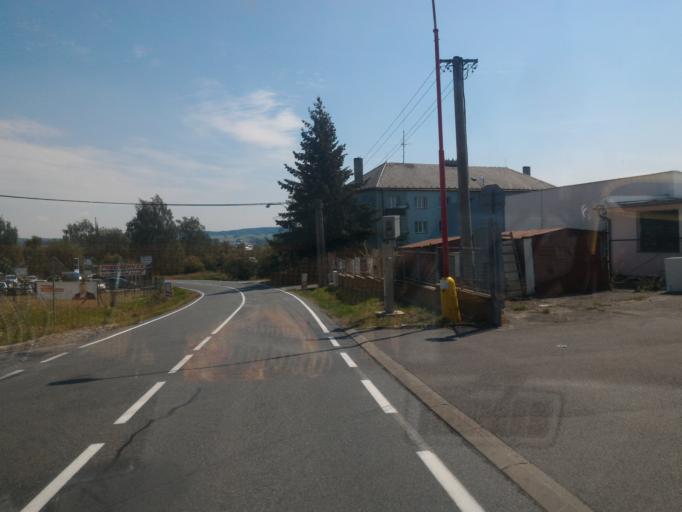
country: CZ
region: Pardubicky
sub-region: Okres Chrudim
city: Hlinsko
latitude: 49.7625
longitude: 15.8930
